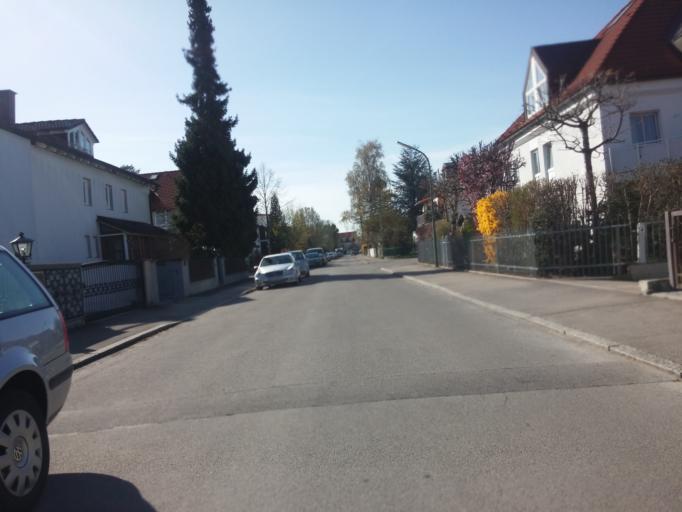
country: DE
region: Bavaria
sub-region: Upper Bavaria
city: Neubiberg
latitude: 48.0810
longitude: 11.6696
